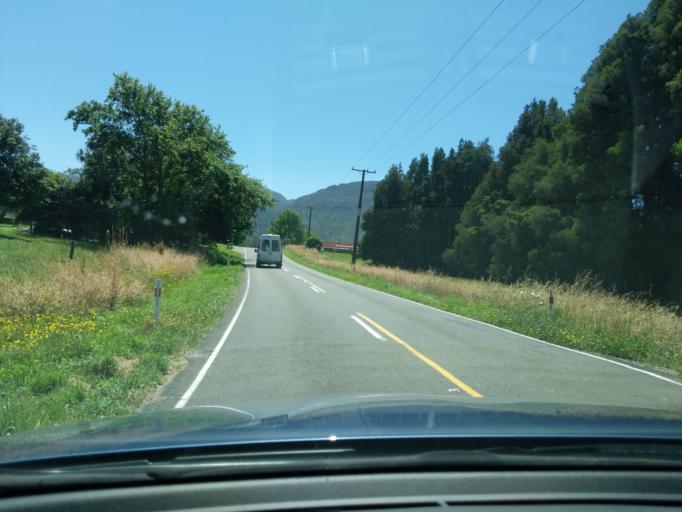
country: NZ
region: Tasman
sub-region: Tasman District
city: Takaka
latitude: -40.7041
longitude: 172.6357
